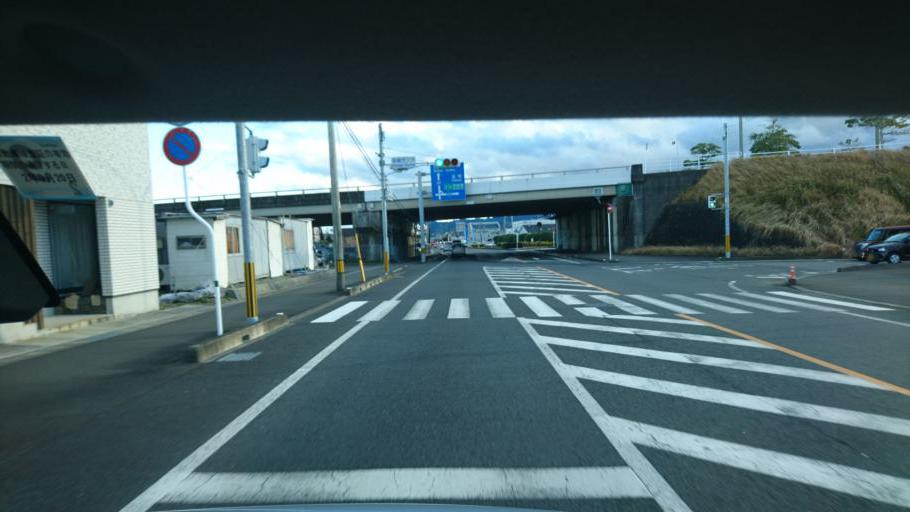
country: JP
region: Miyazaki
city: Miyazaki-shi
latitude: 31.8679
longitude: 131.4318
